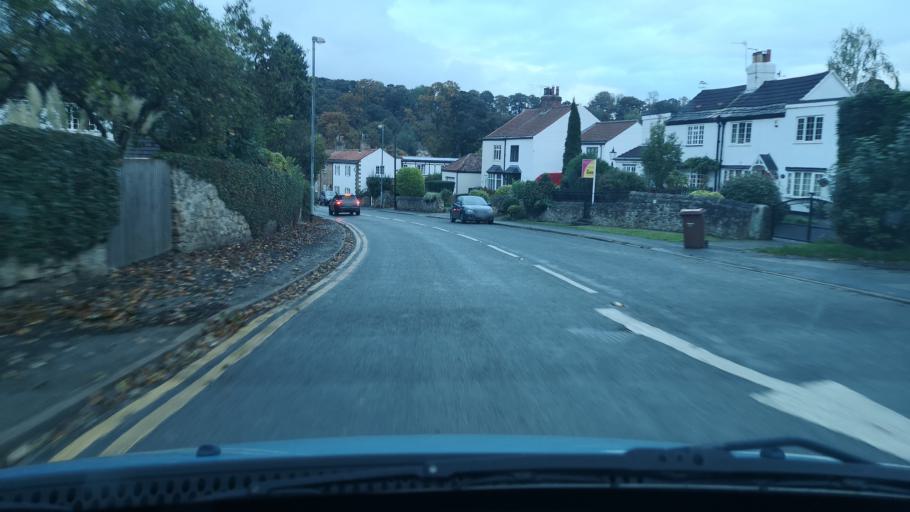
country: GB
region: England
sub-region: City and Borough of Wakefield
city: Darrington
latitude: 53.6484
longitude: -1.2635
